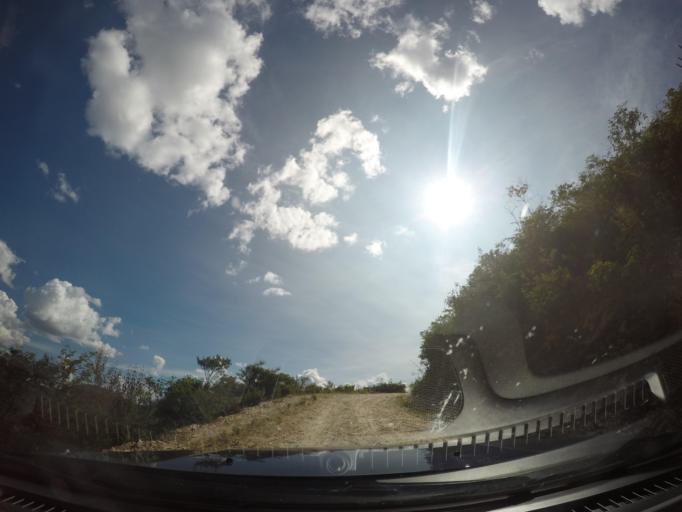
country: BR
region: Bahia
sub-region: Barra Da Estiva
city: Barra da Estiva
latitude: -13.2135
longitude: -41.5925
